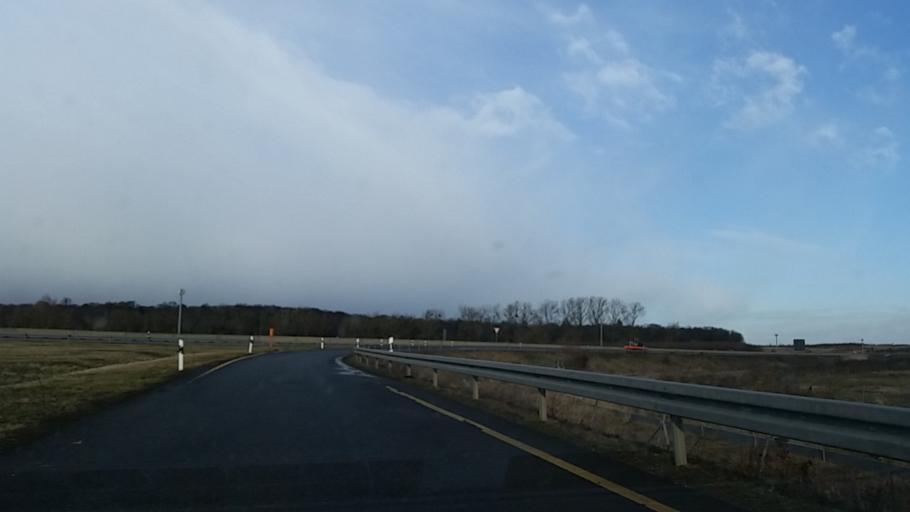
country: DE
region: Lower Saxony
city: Cremlingen
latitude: 52.2552
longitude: 10.6610
